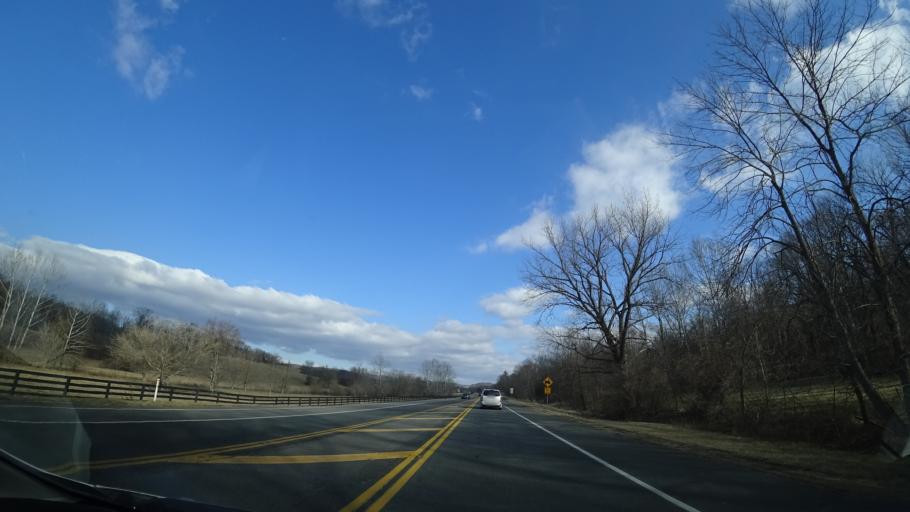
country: US
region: Virginia
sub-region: Fauquier County
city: Marshall
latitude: 38.9367
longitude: -77.9341
